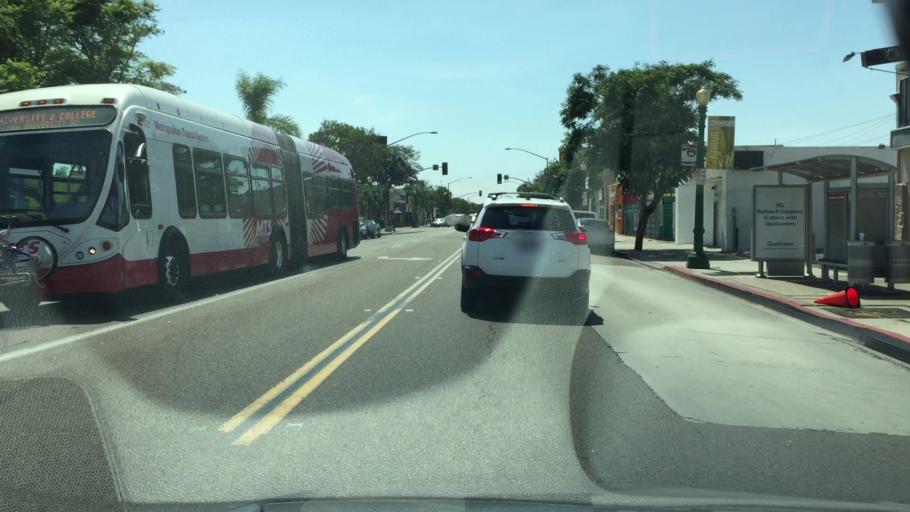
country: US
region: California
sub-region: San Diego County
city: San Diego
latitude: 32.7498
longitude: -117.1157
